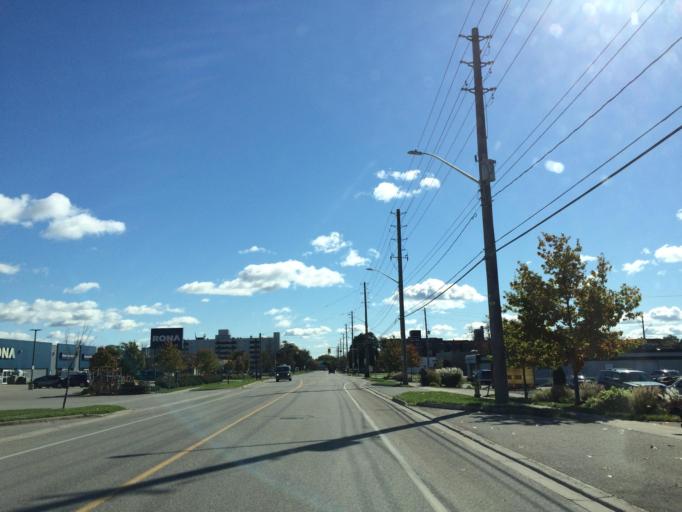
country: CA
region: Ontario
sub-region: Wellington County
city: Guelph
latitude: 43.5474
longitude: -80.2766
